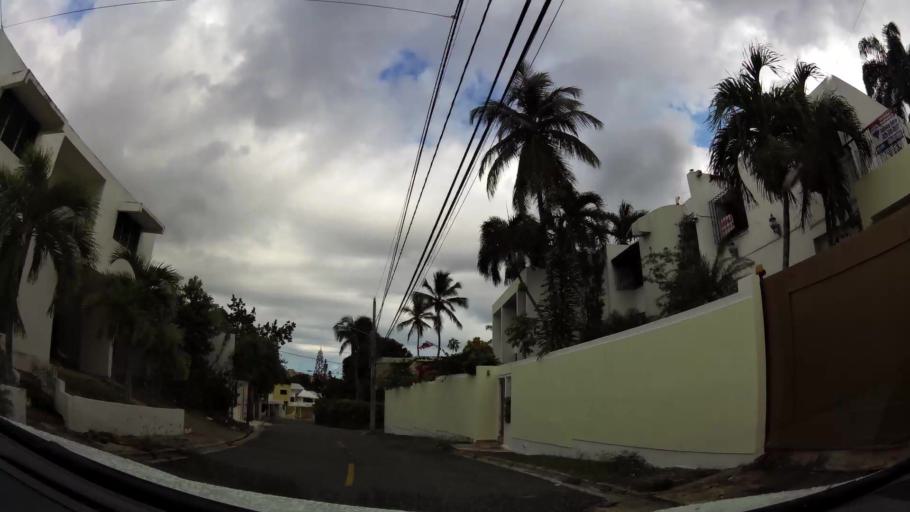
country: DO
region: Nacional
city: La Agustina
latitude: 18.4966
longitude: -69.9388
